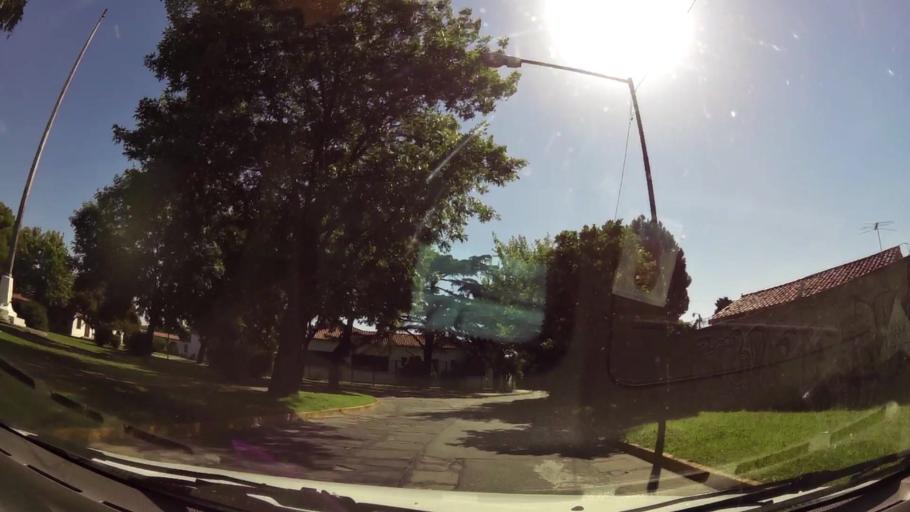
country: AR
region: Buenos Aires
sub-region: Partido de San Isidro
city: San Isidro
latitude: -34.4705
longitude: -58.5301
